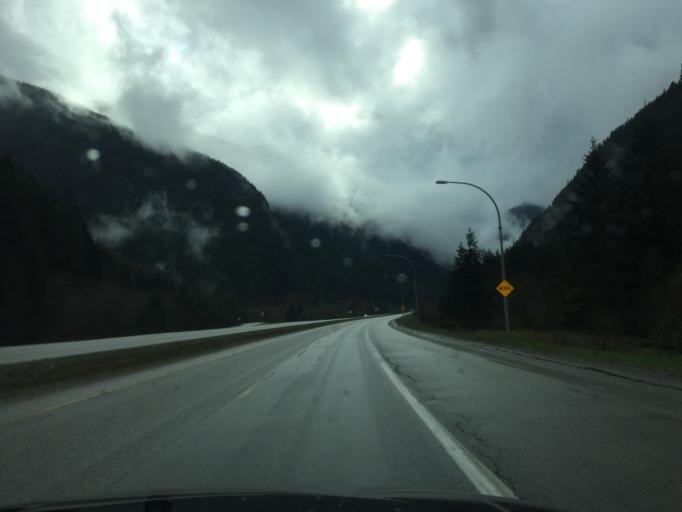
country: CA
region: British Columbia
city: Hope
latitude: 49.4521
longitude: -121.2629
